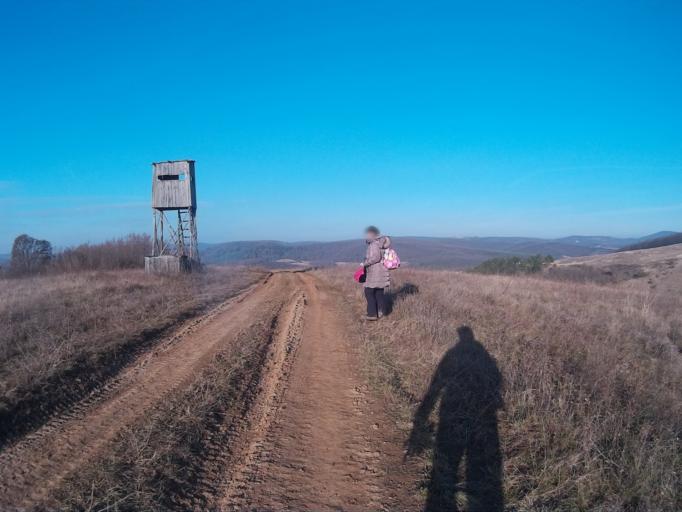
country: HU
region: Nograd
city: Bercel
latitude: 47.9684
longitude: 19.4401
